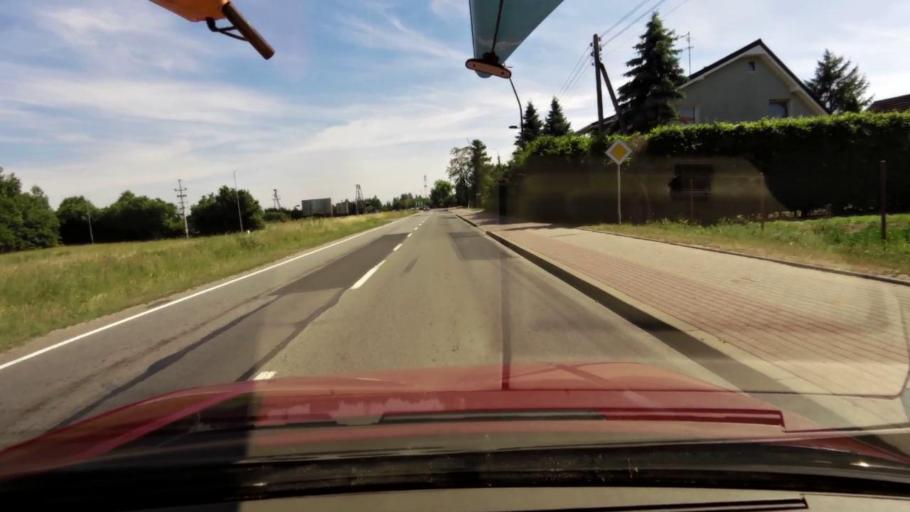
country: PL
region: Pomeranian Voivodeship
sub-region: Powiat slupski
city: Kobylnica
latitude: 54.4357
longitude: 16.9988
